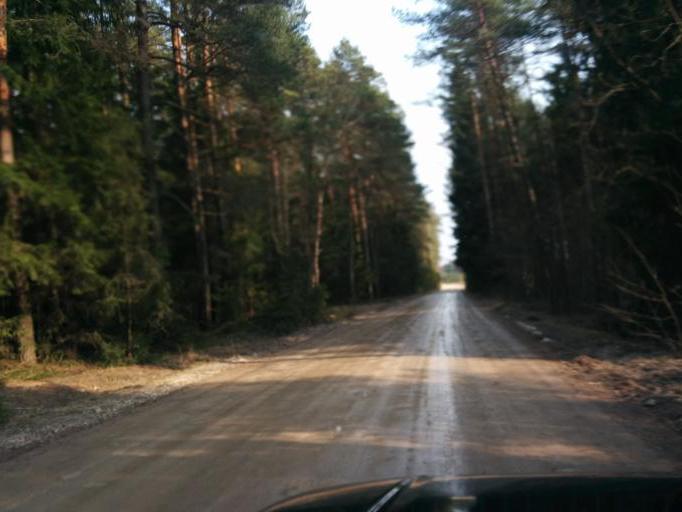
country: LV
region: Olaine
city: Olaine
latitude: 56.7888
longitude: 24.0482
